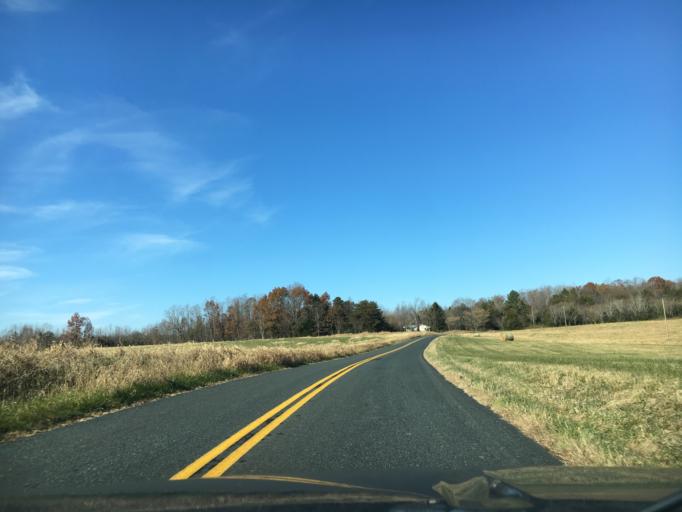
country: US
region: Virginia
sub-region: Buckingham County
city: Buckingham
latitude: 37.4242
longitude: -78.6127
